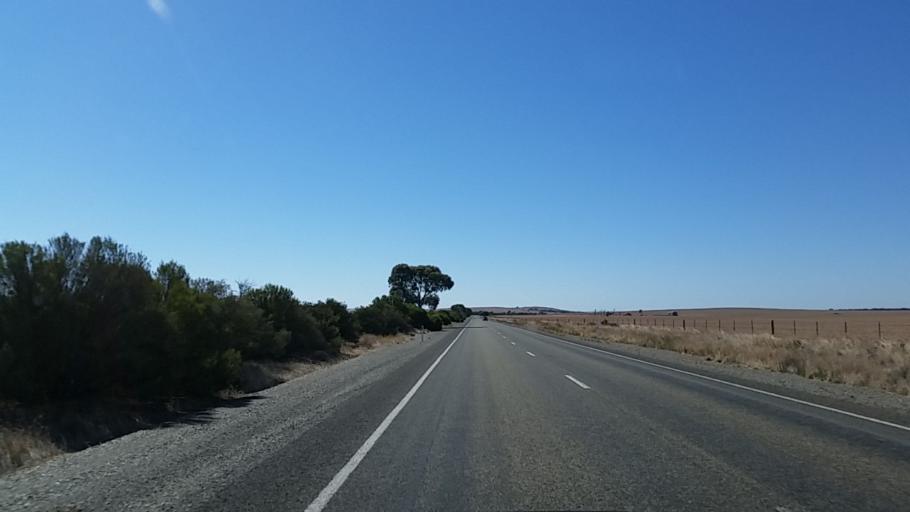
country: AU
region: South Australia
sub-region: Northern Areas
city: Jamestown
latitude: -33.2540
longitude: 138.8718
